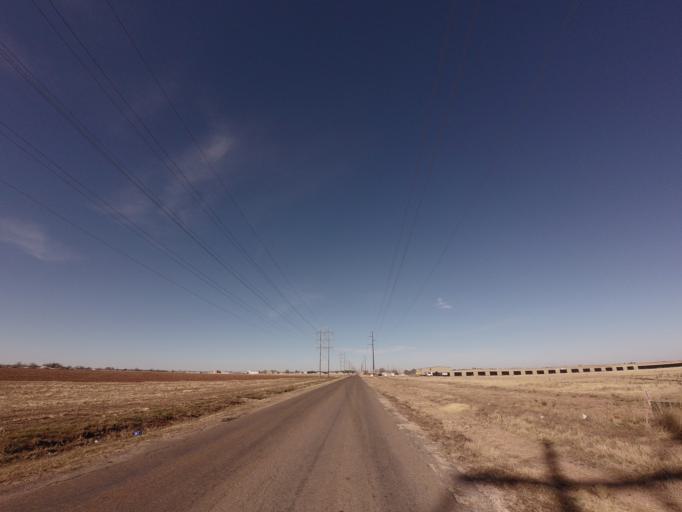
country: US
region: New Mexico
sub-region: Curry County
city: Clovis
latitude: 34.3994
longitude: -103.1433
